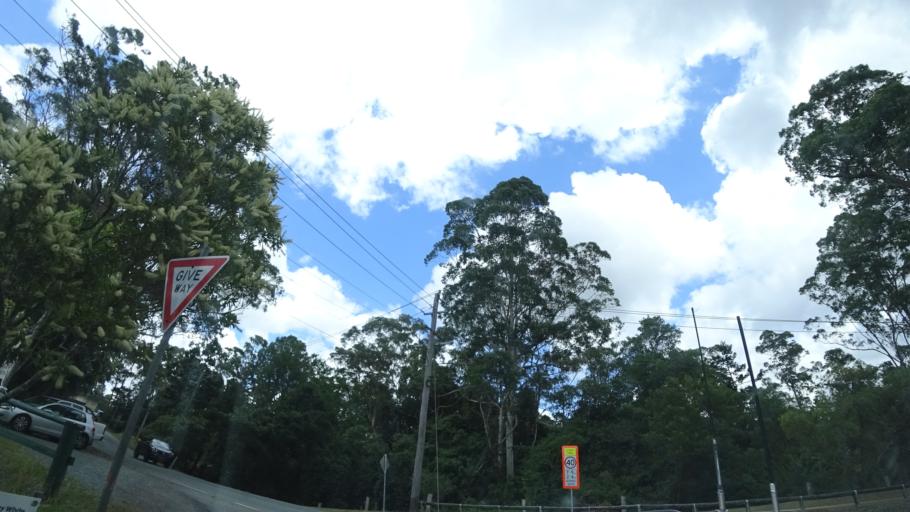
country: AU
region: Queensland
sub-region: Moreton Bay
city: Highvale
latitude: -27.3970
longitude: 152.7839
